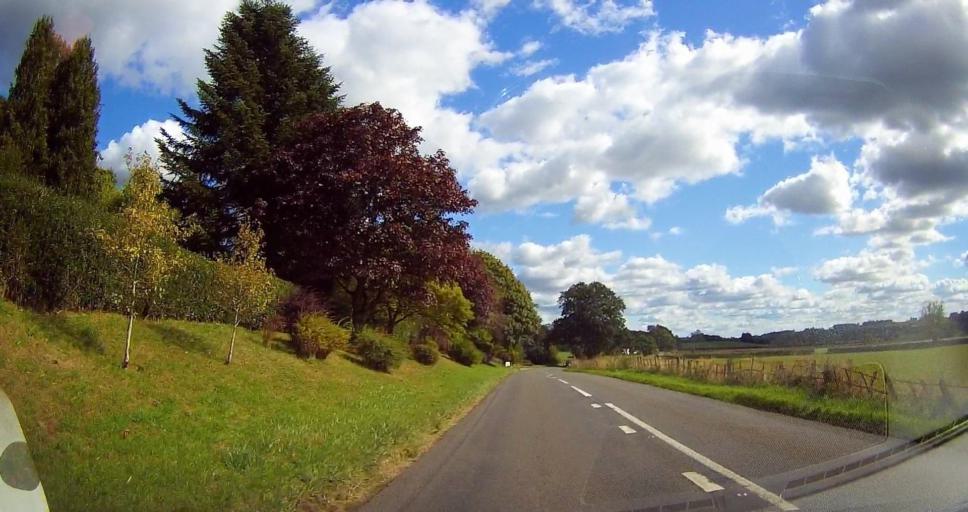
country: GB
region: England
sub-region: Staffordshire
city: Standon
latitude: 52.9554
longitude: -2.3692
